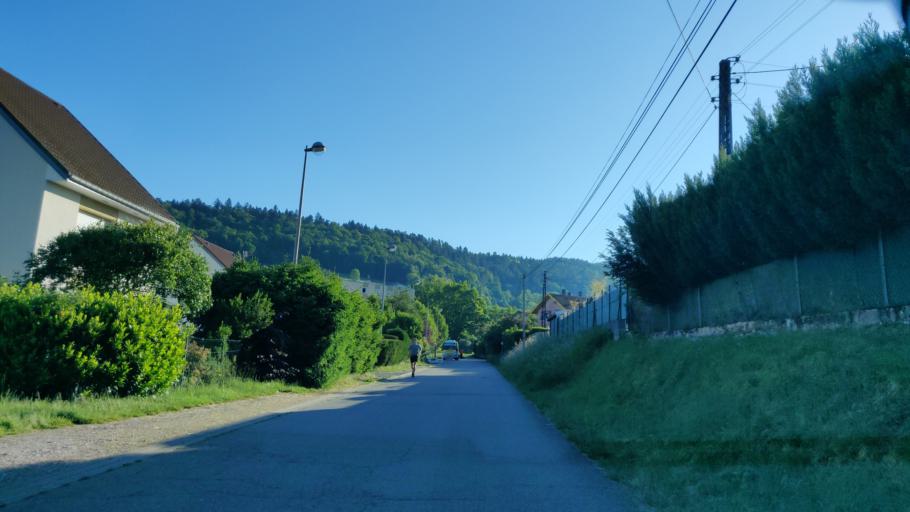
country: FR
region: Lorraine
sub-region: Departement des Vosges
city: Saint-Die-des-Vosges
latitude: 48.2948
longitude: 6.9613
